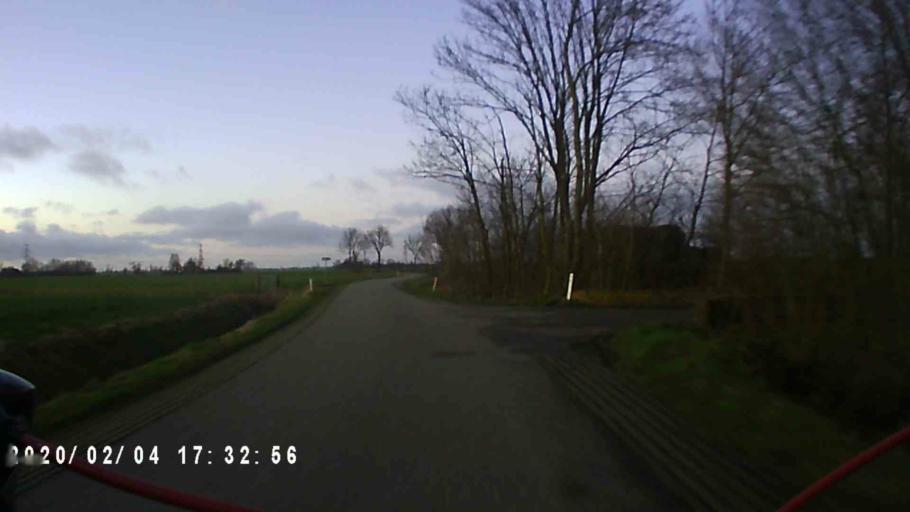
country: NL
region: Groningen
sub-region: Gemeente Zuidhorn
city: Aduard
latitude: 53.2816
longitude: 6.4980
